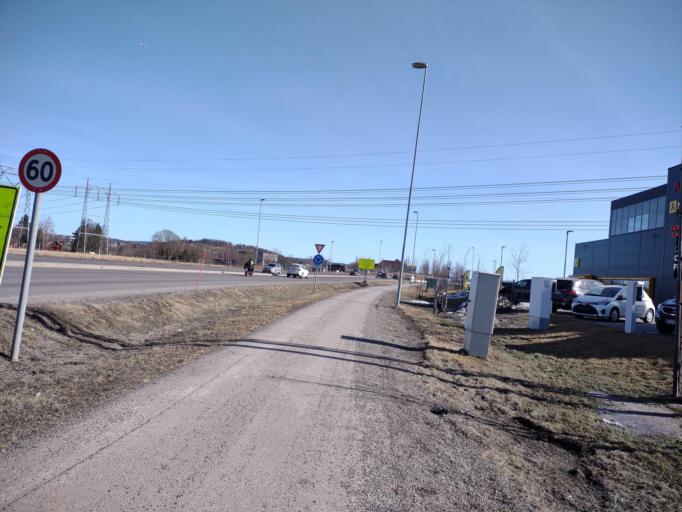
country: NO
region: Akershus
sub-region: Lorenskog
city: Kjenn
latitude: 59.9810
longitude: 10.9892
